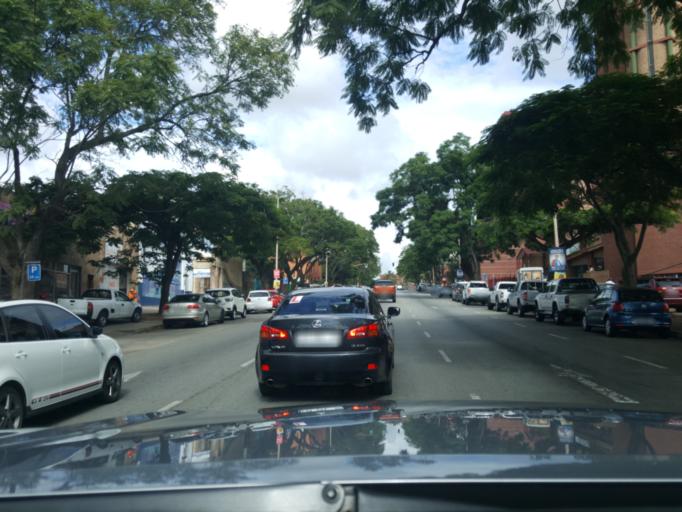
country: ZA
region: Mpumalanga
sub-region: Ehlanzeni District
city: Nelspruit
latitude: -25.4713
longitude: 30.9813
